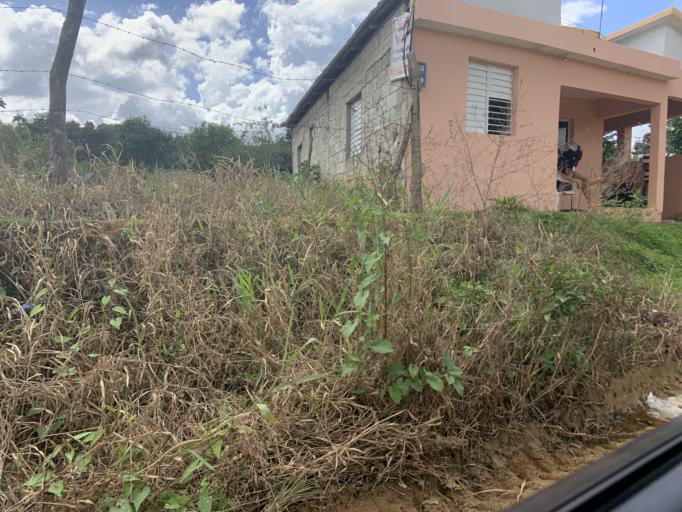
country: DO
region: Monte Plata
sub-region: Yamasa
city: Yamasa
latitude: 18.7812
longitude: -70.0270
